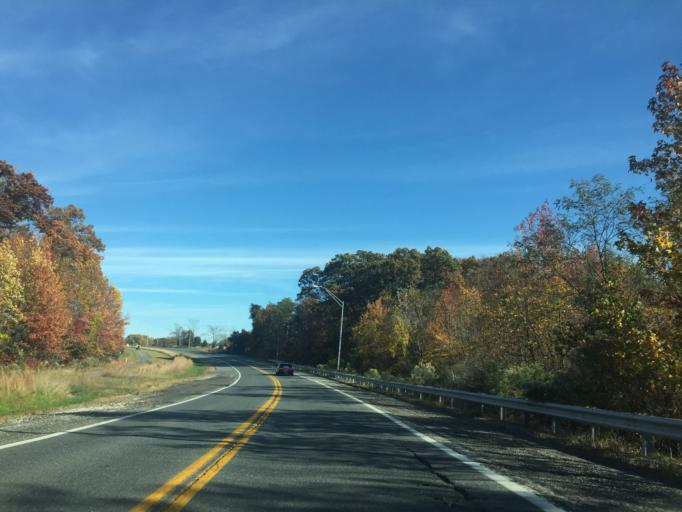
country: US
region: Maryland
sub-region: Baltimore County
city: Overlea
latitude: 39.3624
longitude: -76.4961
